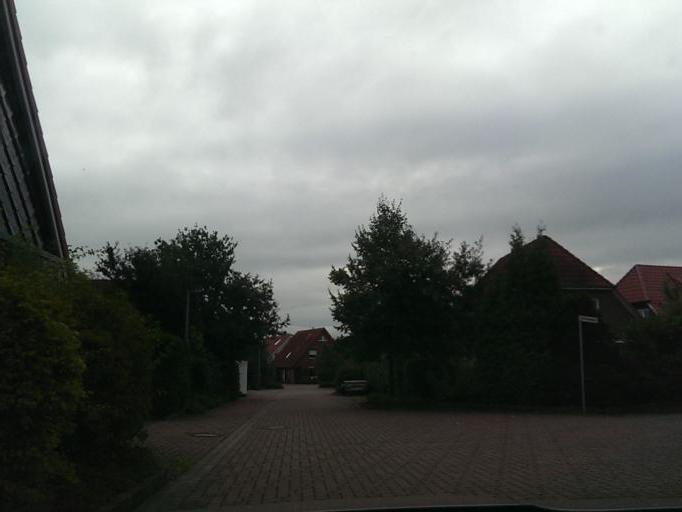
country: DE
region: Lower Saxony
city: Elze
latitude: 52.5271
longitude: 9.7375
